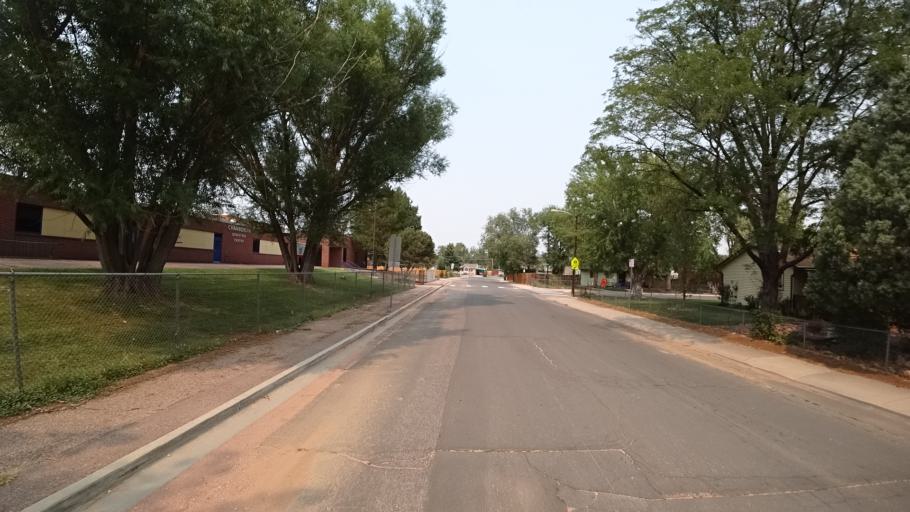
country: US
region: Colorado
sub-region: El Paso County
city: Stratmoor
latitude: 38.7978
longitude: -104.8087
